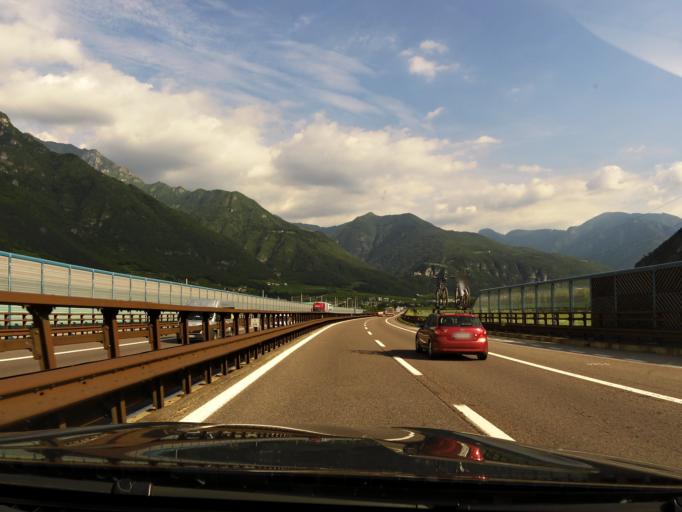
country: IT
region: Trentino-Alto Adige
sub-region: Provincia di Trento
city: Marco
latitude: 45.8072
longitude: 11.0148
